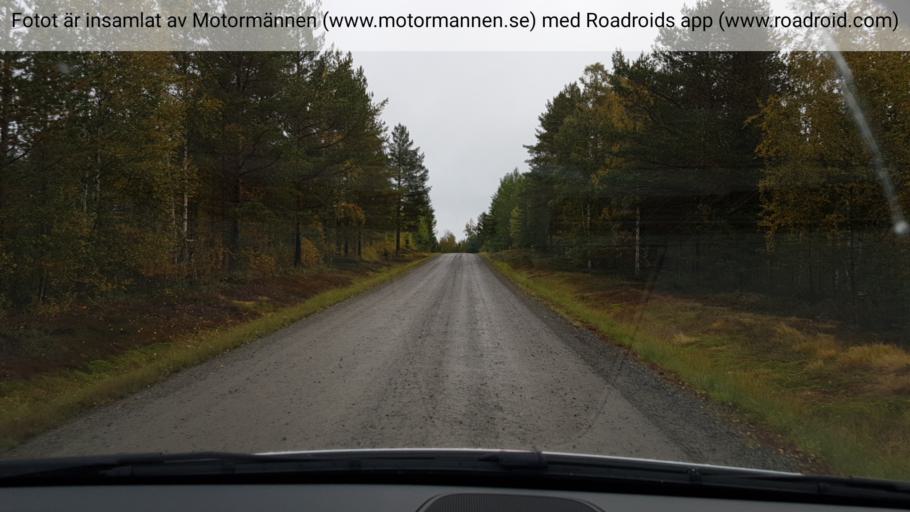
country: SE
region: Vaesterbotten
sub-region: Umea Kommun
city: Ersmark
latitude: 64.1138
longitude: 20.3528
